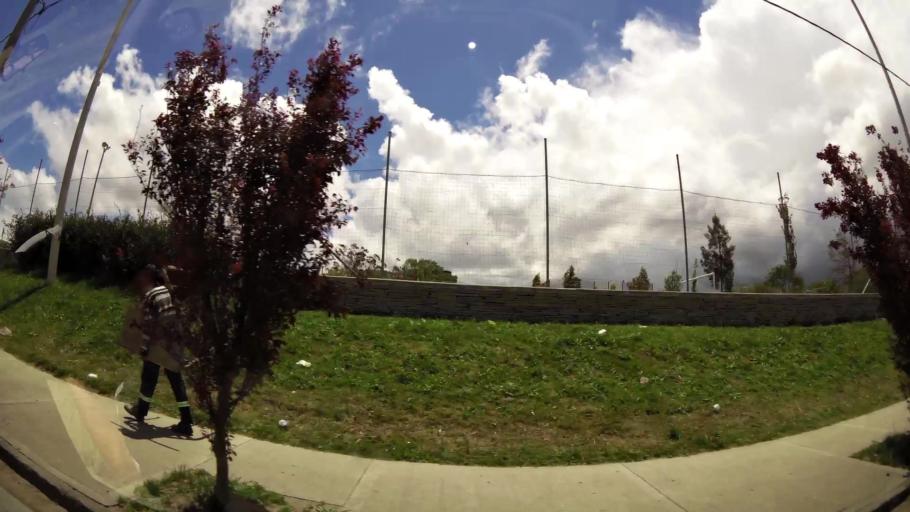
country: UY
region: Montevideo
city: Montevideo
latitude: -34.8360
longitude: -56.1730
